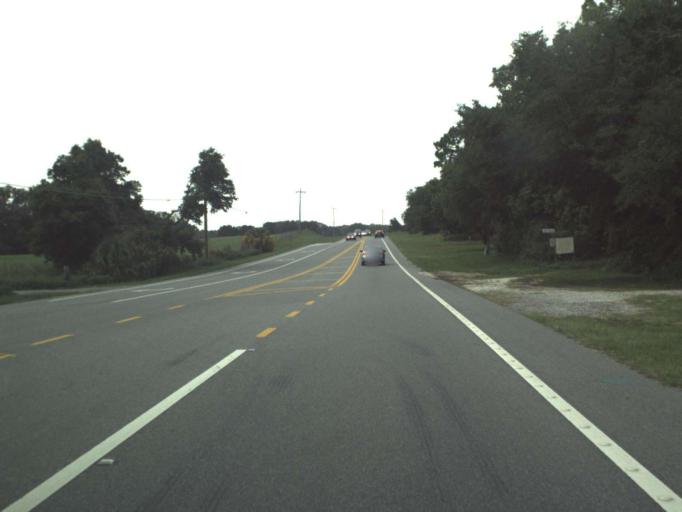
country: US
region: Florida
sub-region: Sumter County
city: Lake Panasoffkee
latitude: 28.7344
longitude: -82.0697
